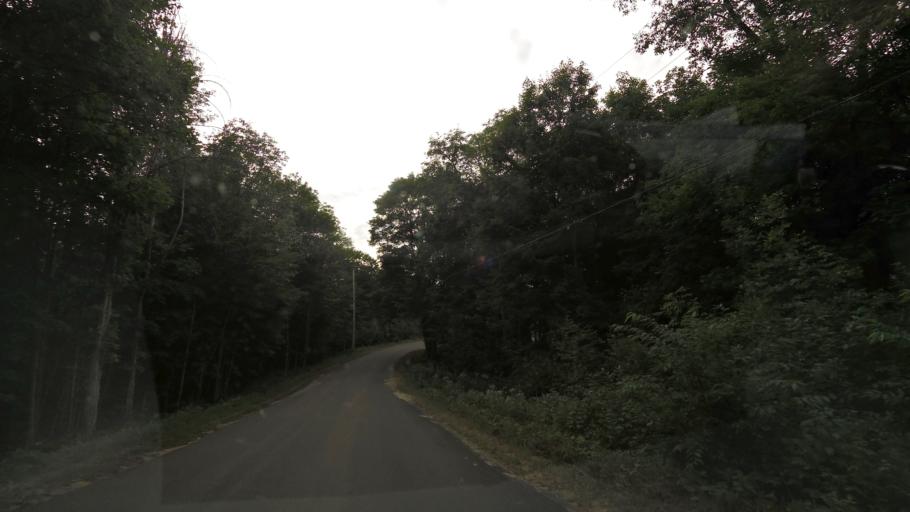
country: CA
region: Ontario
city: Bancroft
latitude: 45.0426
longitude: -78.4964
